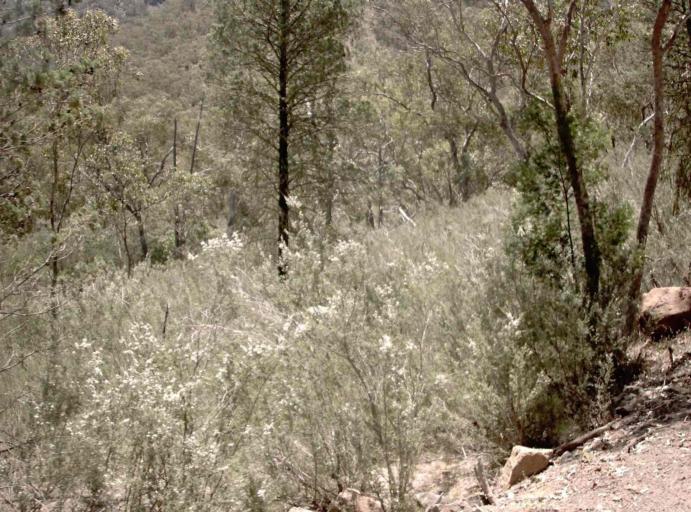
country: AU
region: New South Wales
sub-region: Snowy River
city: Jindabyne
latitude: -37.0782
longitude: 148.4622
